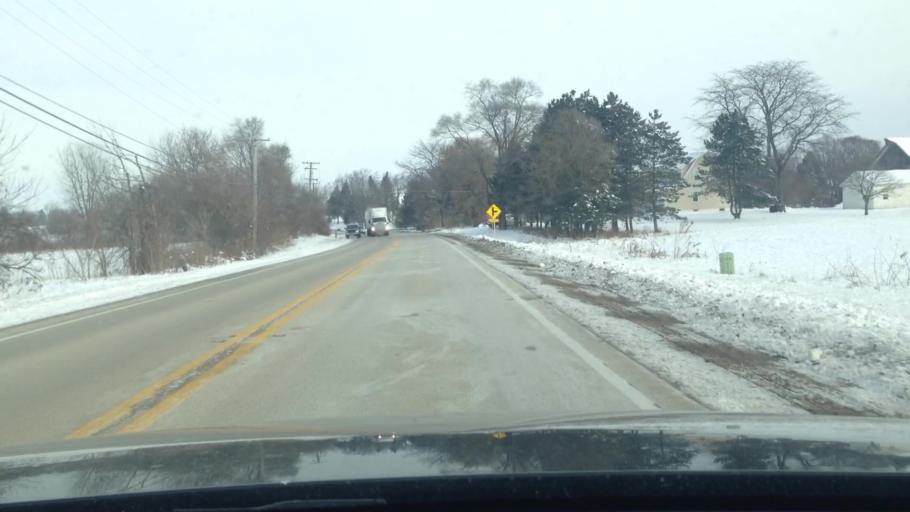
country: US
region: Illinois
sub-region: McHenry County
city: Woodstock
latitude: 42.3516
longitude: -88.4440
